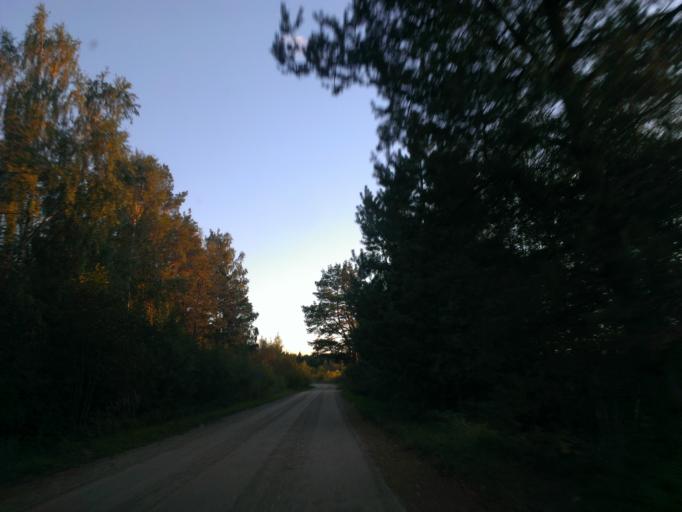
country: LV
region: Incukalns
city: Vangazi
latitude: 57.1068
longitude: 24.5635
